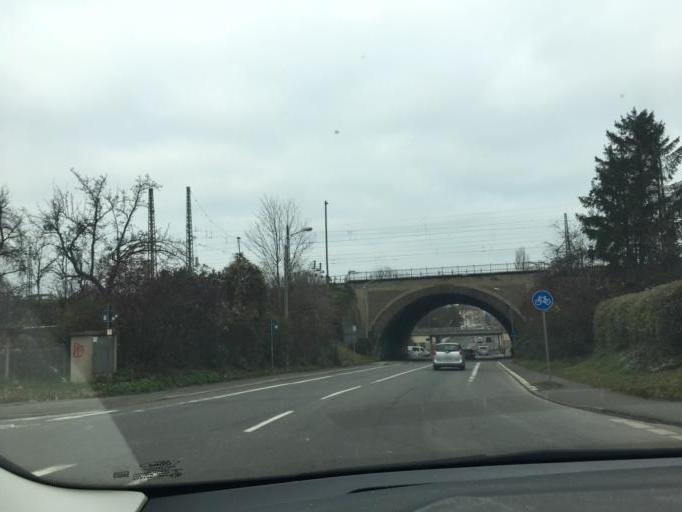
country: DE
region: Saxony
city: Taucha
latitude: 51.3426
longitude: 12.4451
